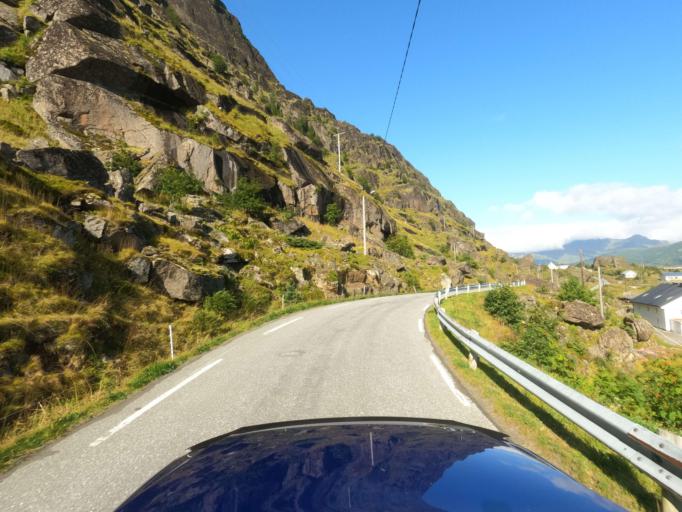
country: NO
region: Nordland
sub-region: Vestvagoy
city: Leknes
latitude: 68.1012
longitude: 13.7270
